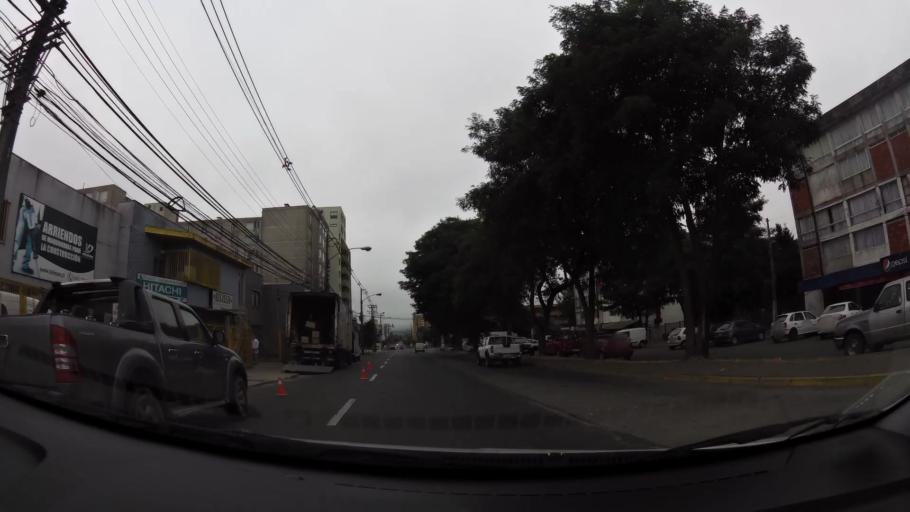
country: CL
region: Biobio
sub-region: Provincia de Concepcion
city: Concepcion
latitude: -36.8180
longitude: -73.0485
